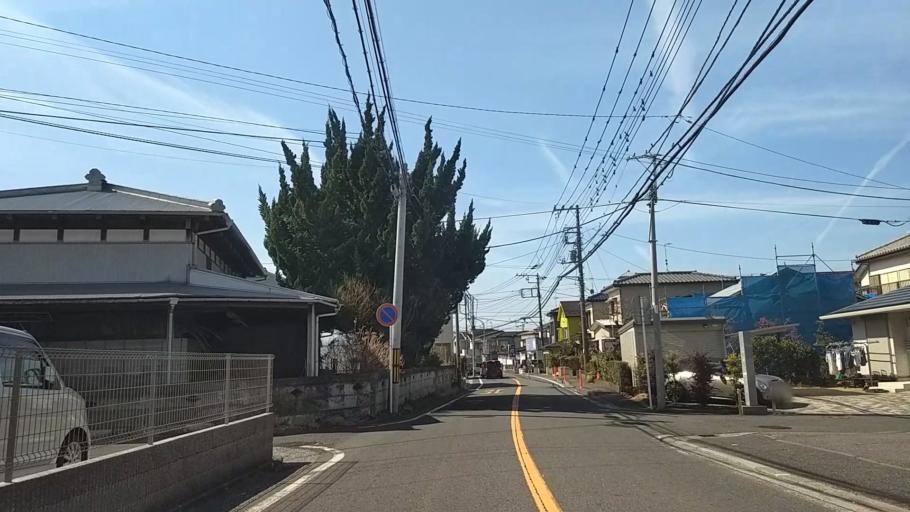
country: JP
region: Kanagawa
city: Fujisawa
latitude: 35.3841
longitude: 139.5049
